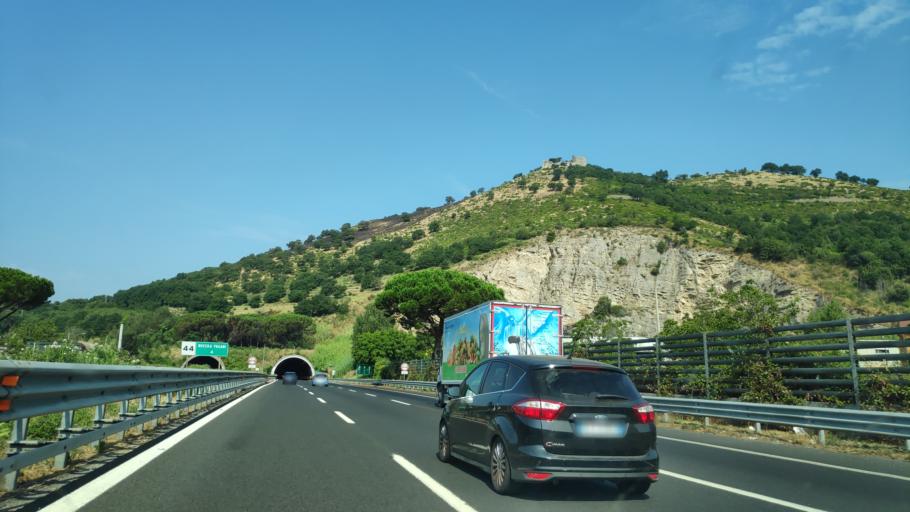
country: IT
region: Campania
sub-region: Provincia di Salerno
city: Lanzara
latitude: 40.7720
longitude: 14.6633
